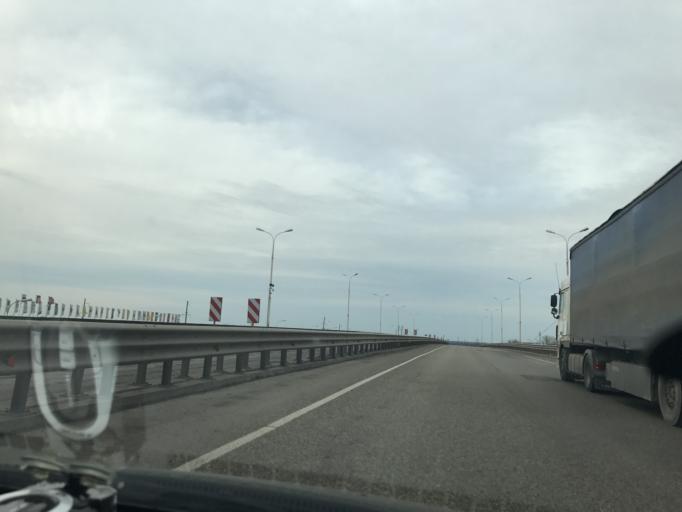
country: RU
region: Krasnodarskiy
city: Glubokiy
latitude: 44.9664
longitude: 41.0589
